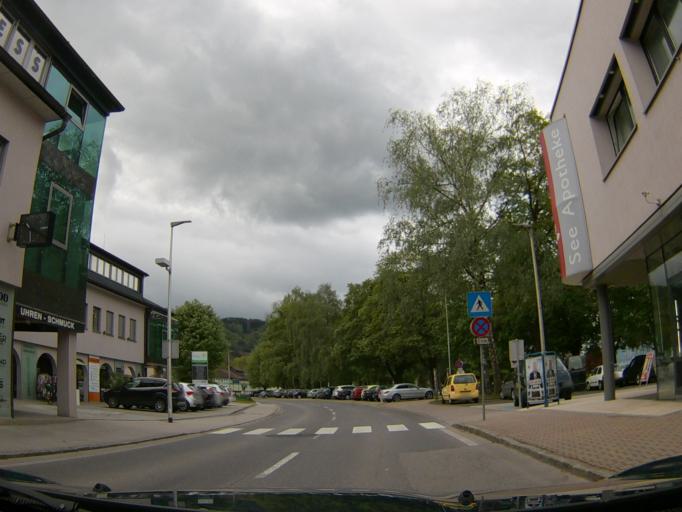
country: AT
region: Upper Austria
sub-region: Politischer Bezirk Vocklabruck
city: Seewalchen
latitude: 47.9462
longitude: 13.5946
